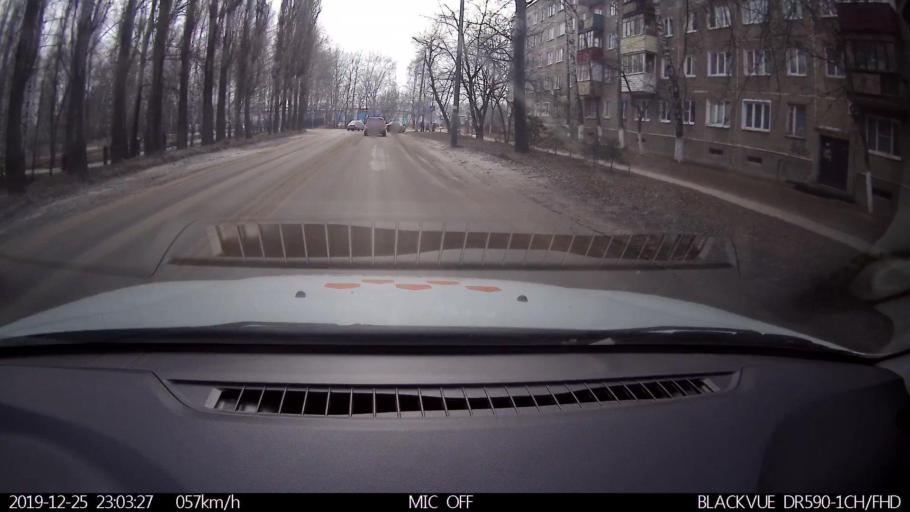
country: RU
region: Nizjnij Novgorod
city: Gorbatovka
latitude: 56.3558
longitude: 43.8208
